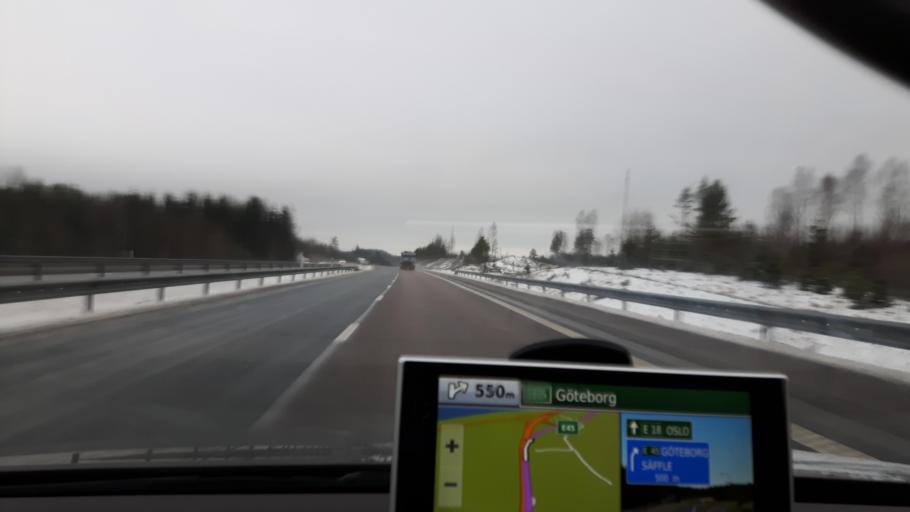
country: SE
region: Vaermland
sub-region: Grums Kommun
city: Slottsbron
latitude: 59.2700
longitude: 13.0102
